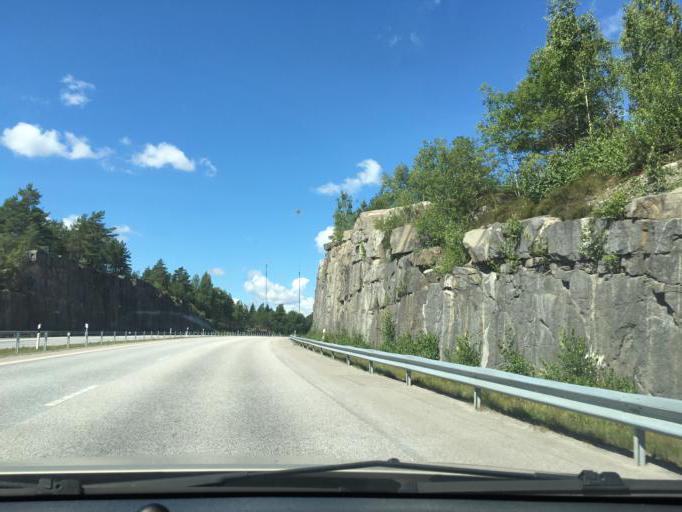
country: SE
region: Stockholm
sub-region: Nacka Kommun
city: Alta
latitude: 59.2930
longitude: 18.2137
